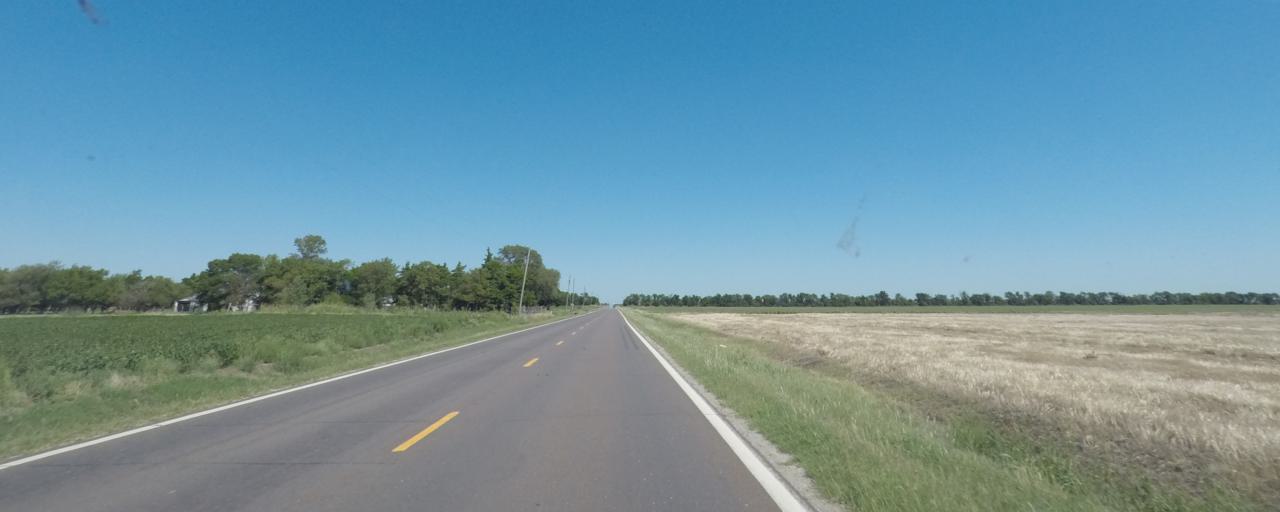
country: US
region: Kansas
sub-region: Sumner County
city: Wellington
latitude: 37.1902
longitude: -97.4022
